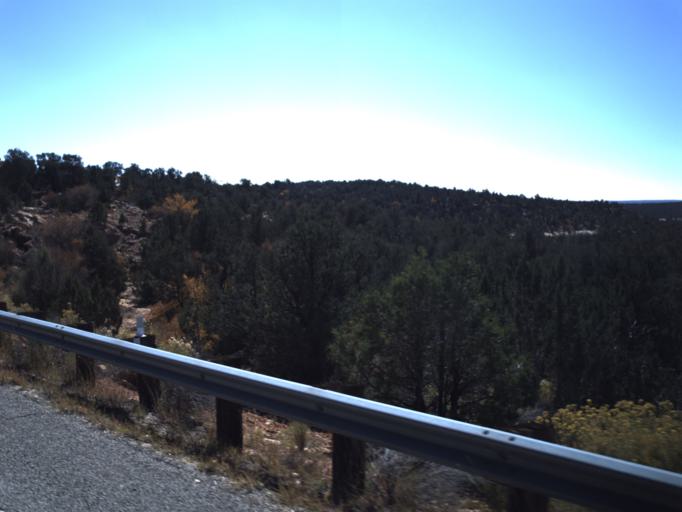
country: US
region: Utah
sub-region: San Juan County
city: Blanding
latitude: 37.5858
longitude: -109.8951
